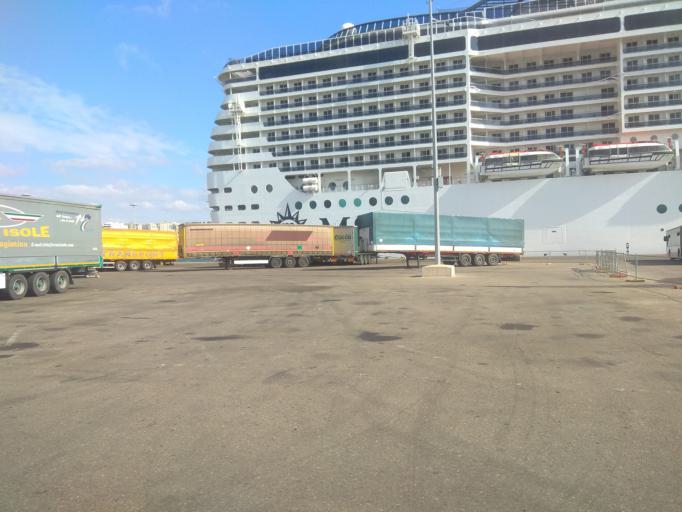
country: IT
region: Sardinia
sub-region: Provincia di Cagliari
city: Cagliari
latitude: 39.2098
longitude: 9.1042
